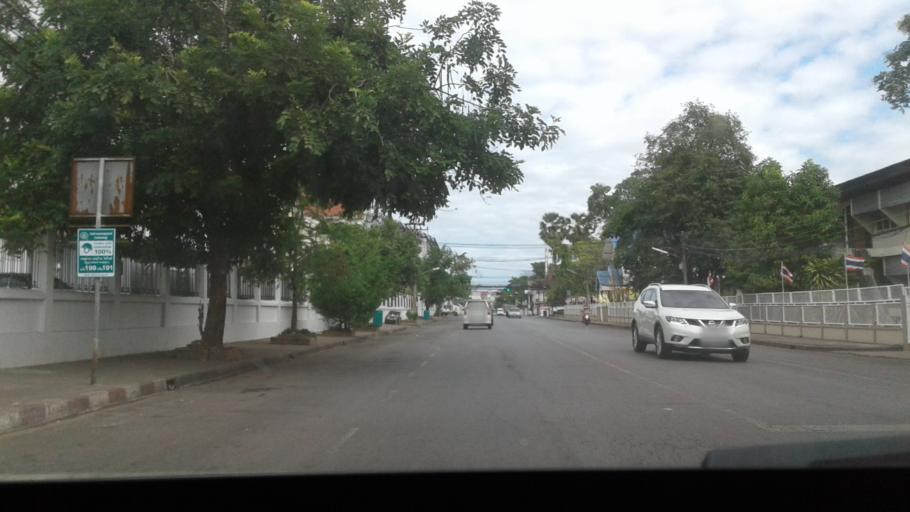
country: TH
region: Changwat Udon Thani
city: Udon Thani
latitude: 17.4137
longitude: 102.7885
